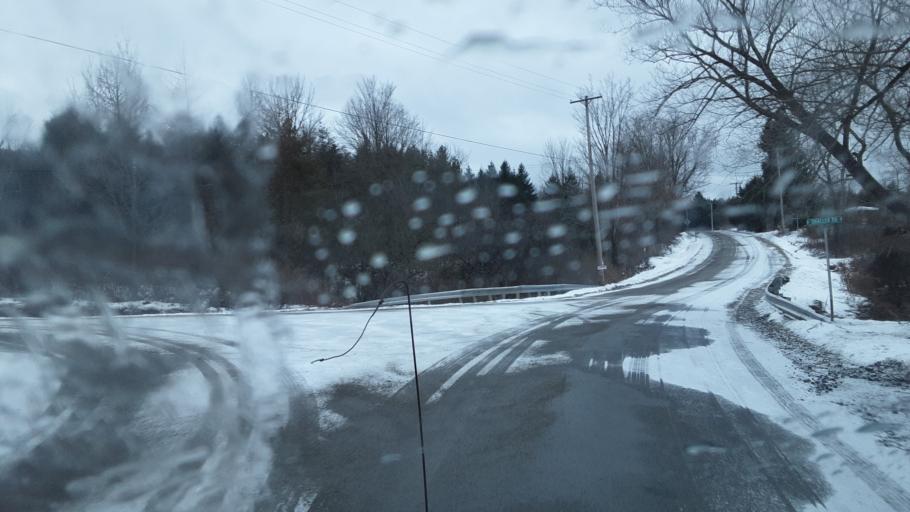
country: US
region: New York
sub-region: Allegany County
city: Friendship
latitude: 42.2978
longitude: -78.1489
